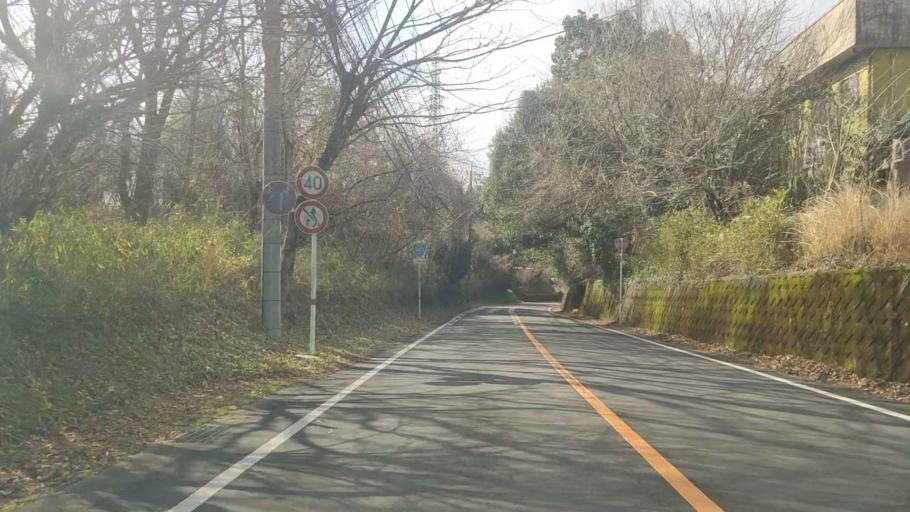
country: JP
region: Kumamoto
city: Hitoyoshi
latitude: 32.2274
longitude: 130.7819
